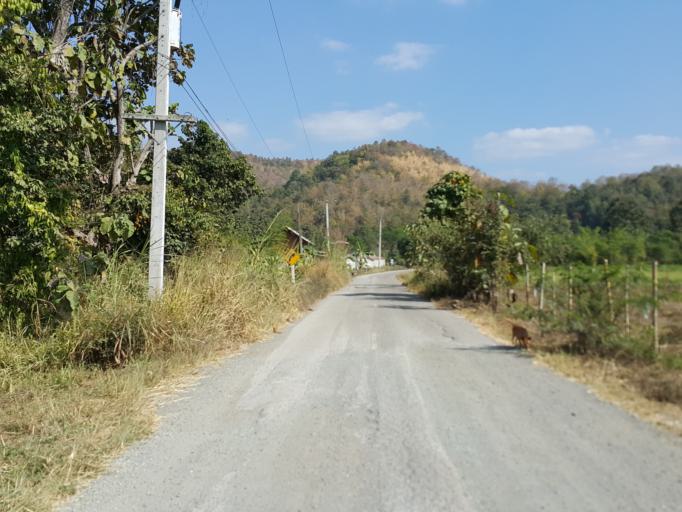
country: TH
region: Chiang Mai
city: Mae On
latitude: 18.8327
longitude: 99.2305
